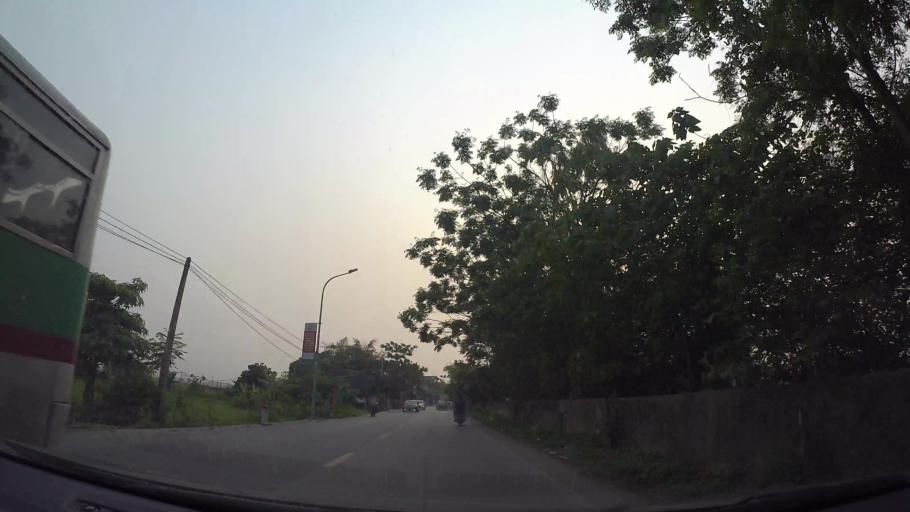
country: VN
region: Ha Noi
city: Thuong Tin
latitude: 20.8699
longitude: 105.8253
